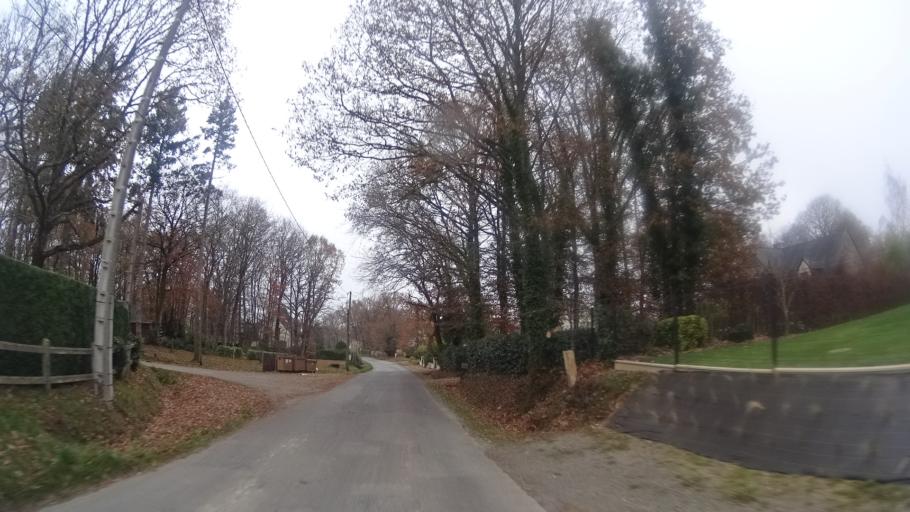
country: FR
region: Brittany
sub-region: Departement d'Ille-et-Vilaine
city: Bains-sur-Oust
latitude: 47.6894
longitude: -2.0789
